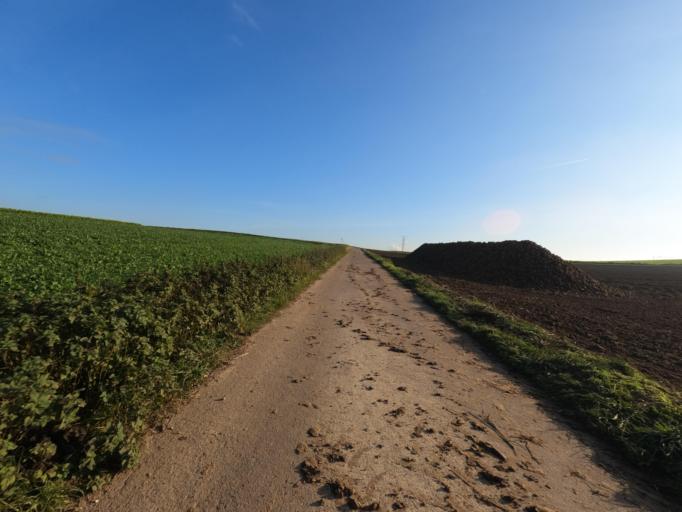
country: DE
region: North Rhine-Westphalia
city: Huckelhoven
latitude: 50.9923
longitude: 6.1942
